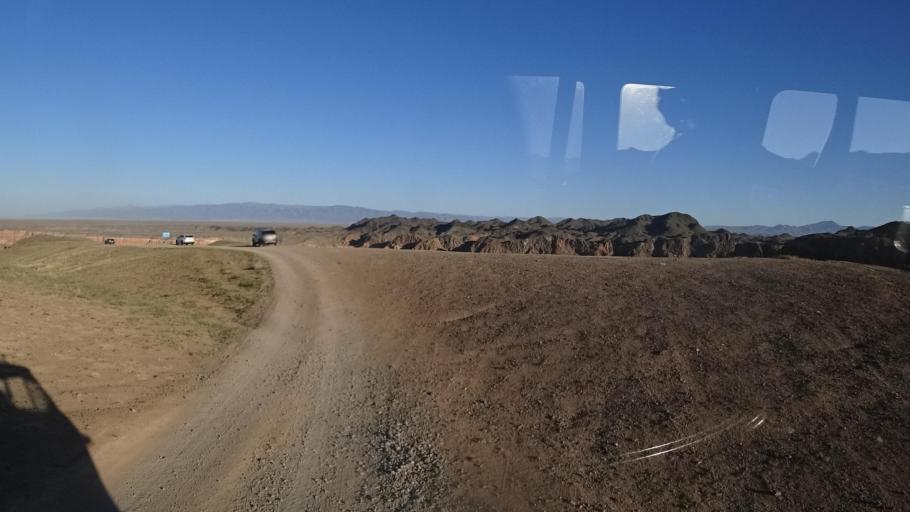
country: KZ
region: Almaty Oblysy
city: Kegen
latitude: 43.3552
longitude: 79.0651
